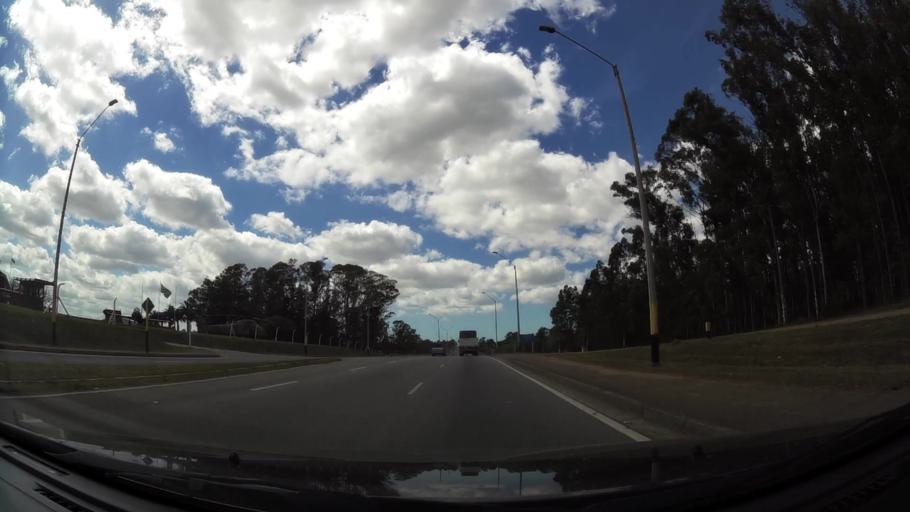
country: UY
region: Canelones
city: Colonia Nicolich
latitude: -34.8081
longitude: -56.0450
